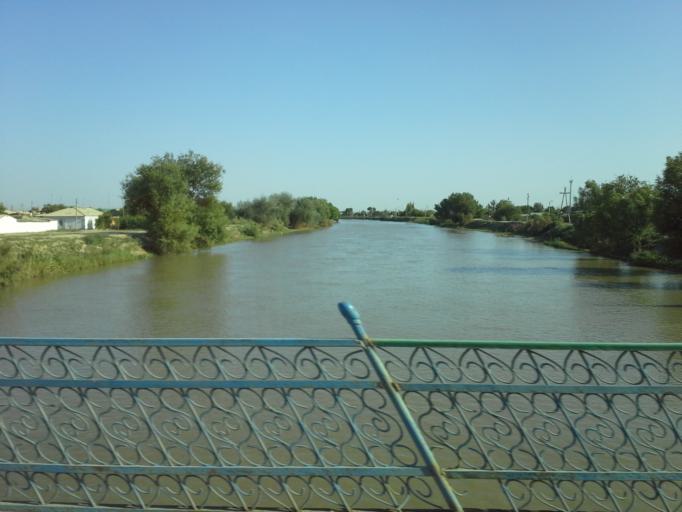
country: TM
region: Dasoguz
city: Dasoguz
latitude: 41.8303
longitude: 59.9805
